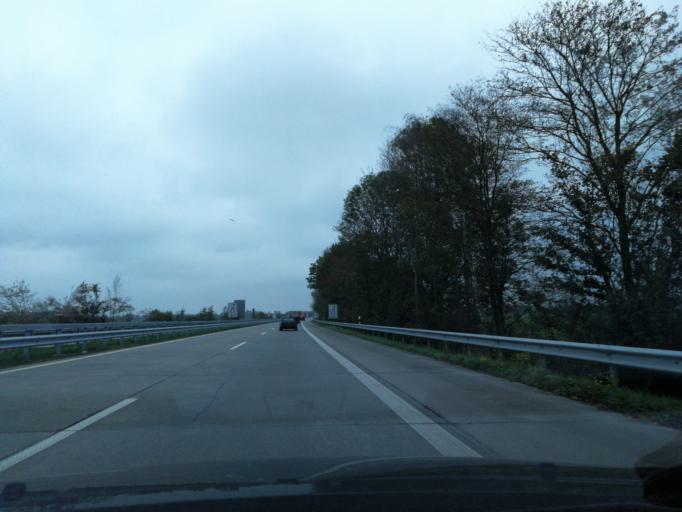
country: DE
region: Lower Saxony
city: Sande
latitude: 53.5317
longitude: 8.0148
